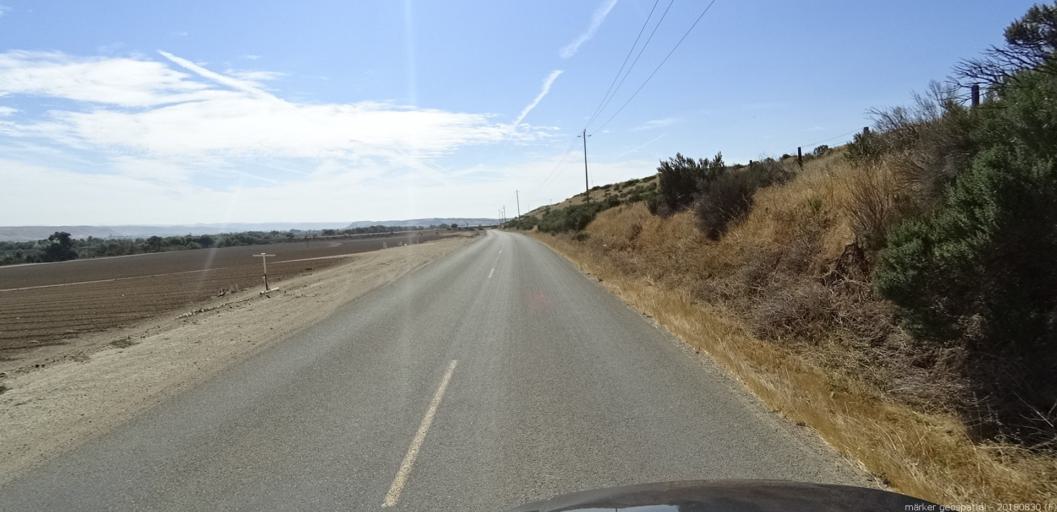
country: US
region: California
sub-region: Monterey County
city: King City
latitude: 36.1078
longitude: -121.0301
